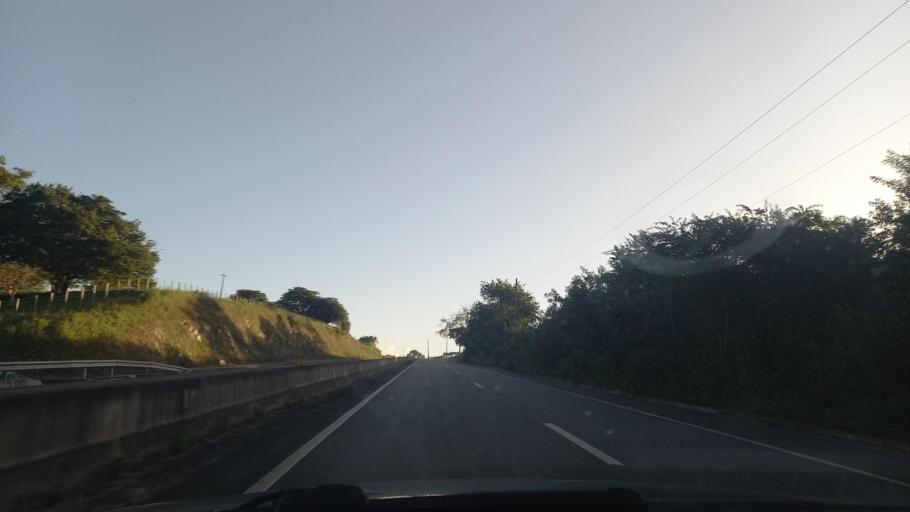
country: BR
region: Alagoas
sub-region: Limoeiro De Anadia
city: Limoeiro de Anadia
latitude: -9.7414
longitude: -36.4968
